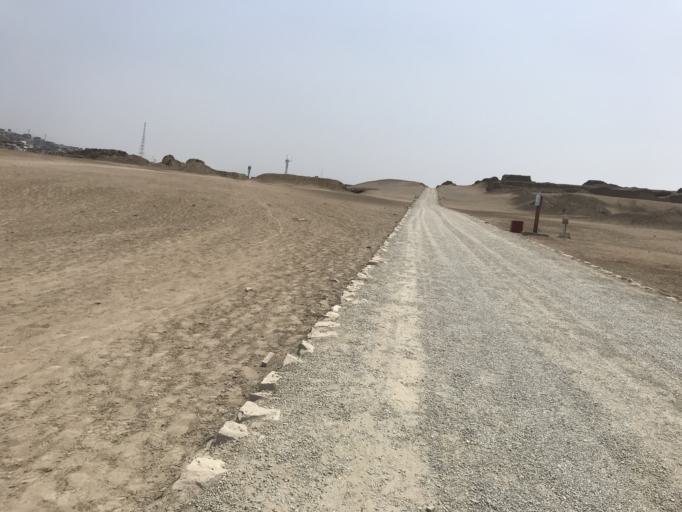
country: PE
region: Lima
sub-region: Lima
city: Punta Hermosa
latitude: -12.2555
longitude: -76.9008
